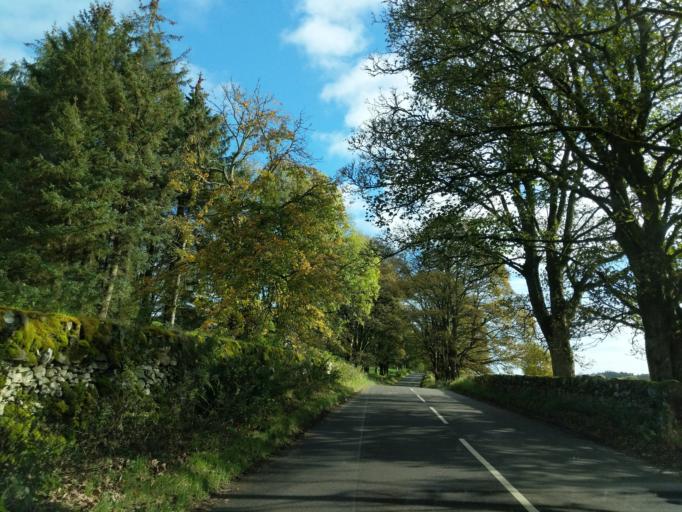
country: GB
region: Scotland
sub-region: Dumfries and Galloway
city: Thornhill
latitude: 55.1944
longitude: -3.9028
